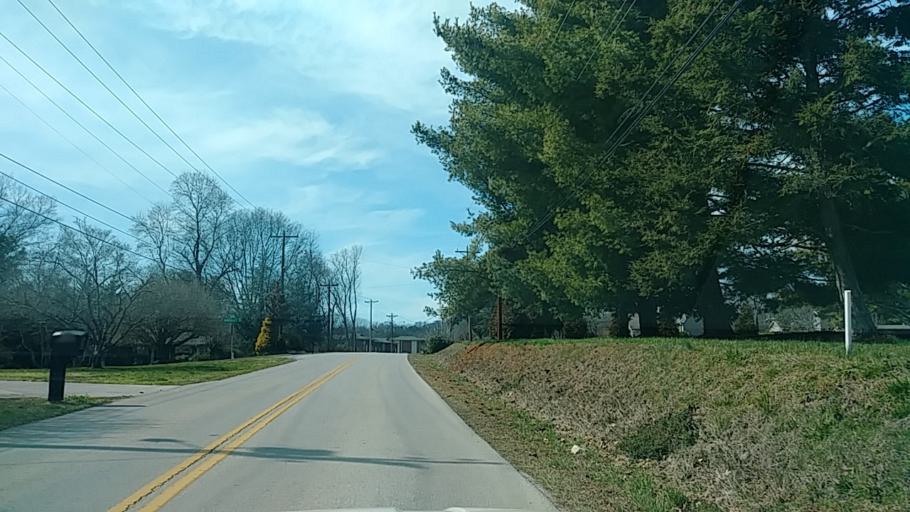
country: US
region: Tennessee
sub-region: Hamblen County
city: Morristown
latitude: 36.2124
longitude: -83.3290
